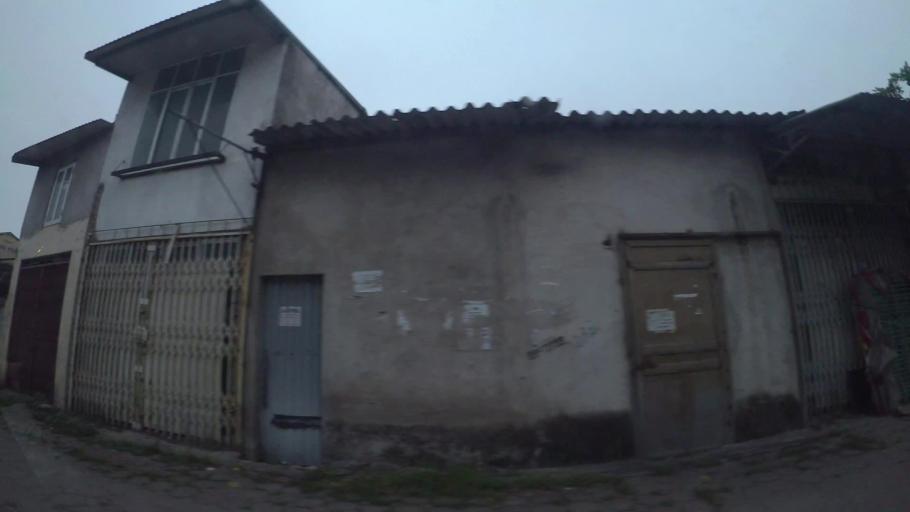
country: VN
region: Ha Noi
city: Hai BaTrung
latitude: 20.9974
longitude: 105.8362
